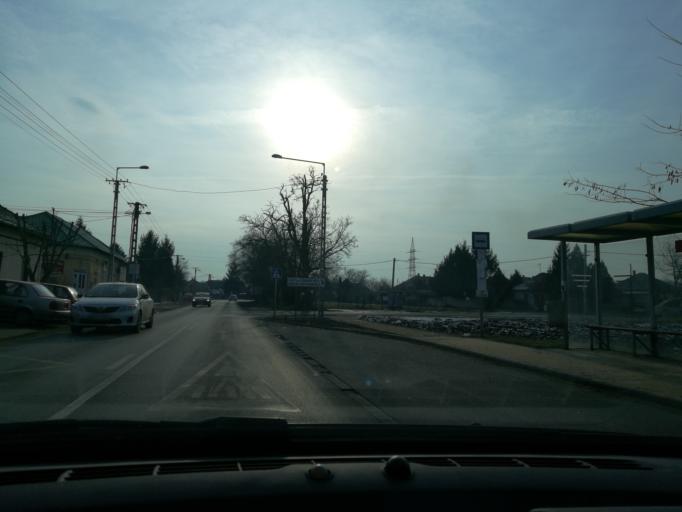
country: HU
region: Szabolcs-Szatmar-Bereg
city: Nyiregyhaza
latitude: 47.9332
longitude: 21.7090
